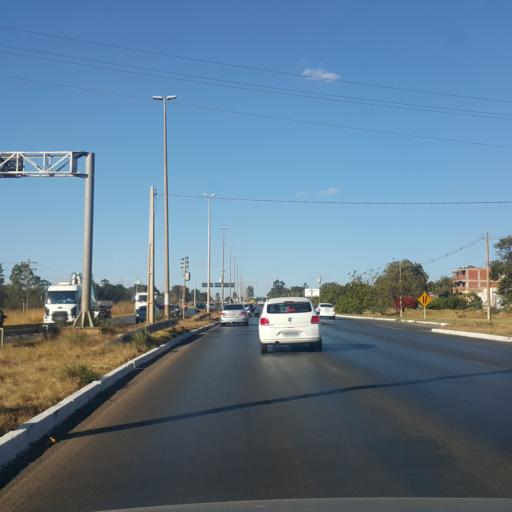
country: BR
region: Federal District
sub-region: Brasilia
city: Brasilia
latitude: -15.7959
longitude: -48.0659
